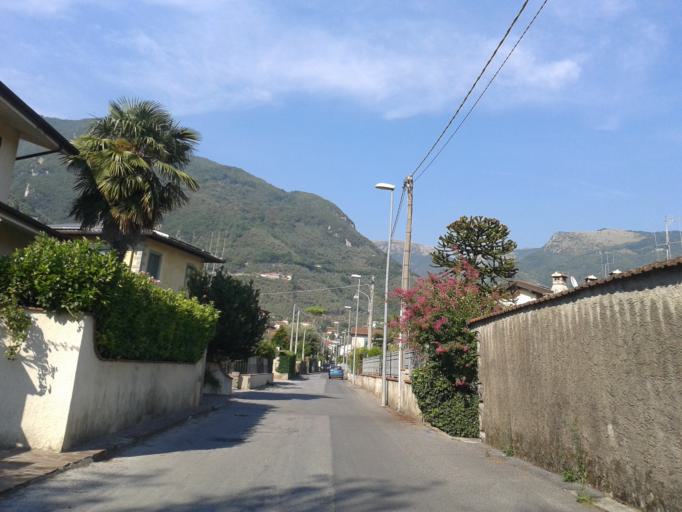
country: IT
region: Tuscany
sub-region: Provincia di Lucca
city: Corsanico-Bargecchia
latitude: 43.9456
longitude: 10.3008
